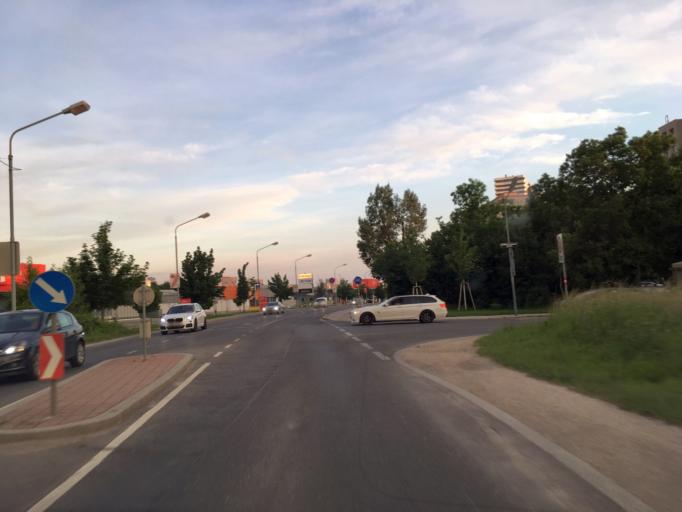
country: AT
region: Lower Austria
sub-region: Politischer Bezirk Wien-Umgebung
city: Gerasdorf bei Wien
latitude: 48.2684
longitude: 16.4565
